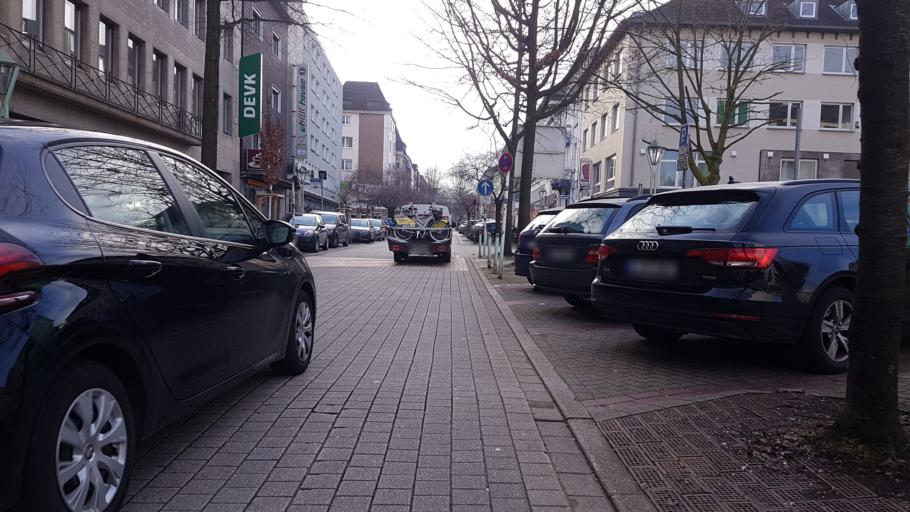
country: DE
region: North Rhine-Westphalia
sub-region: Regierungsbezirk Dusseldorf
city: Essen
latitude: 51.4413
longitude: 7.0061
